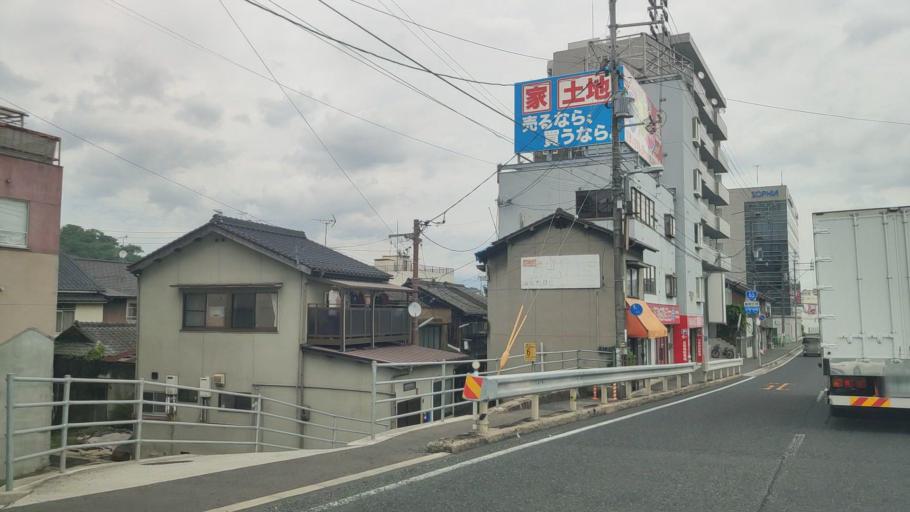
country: JP
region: Okayama
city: Tsuyama
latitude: 35.0577
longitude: 134.0037
